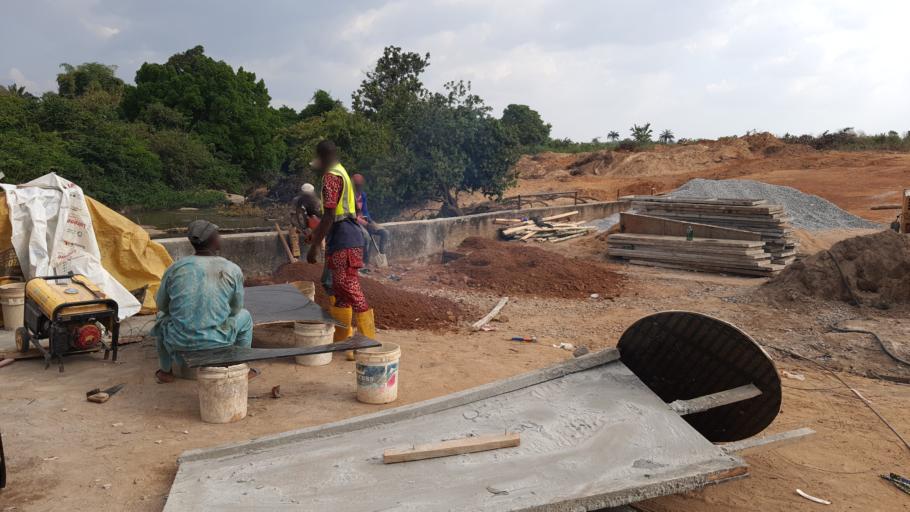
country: NG
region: Osun
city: Iwo
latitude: 7.7374
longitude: 4.0842
